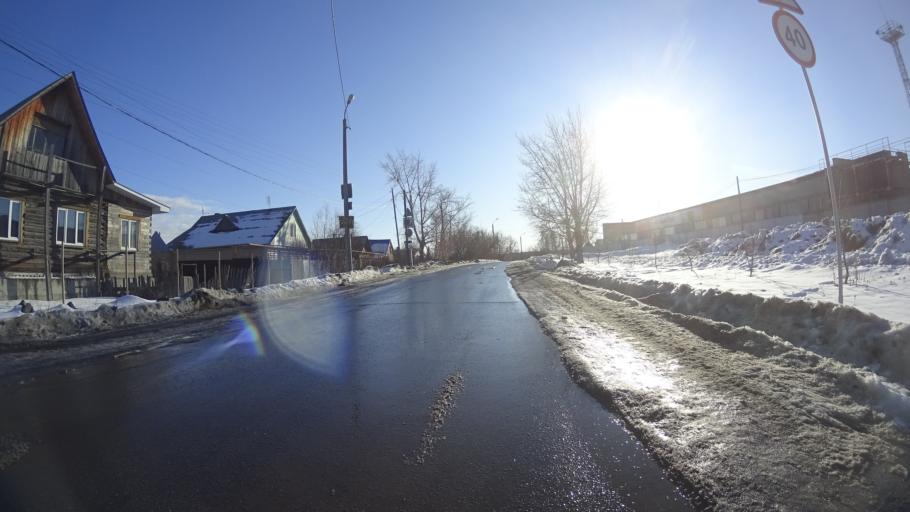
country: RU
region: Chelyabinsk
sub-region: Gorod Chelyabinsk
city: Chelyabinsk
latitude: 55.1496
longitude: 61.3075
